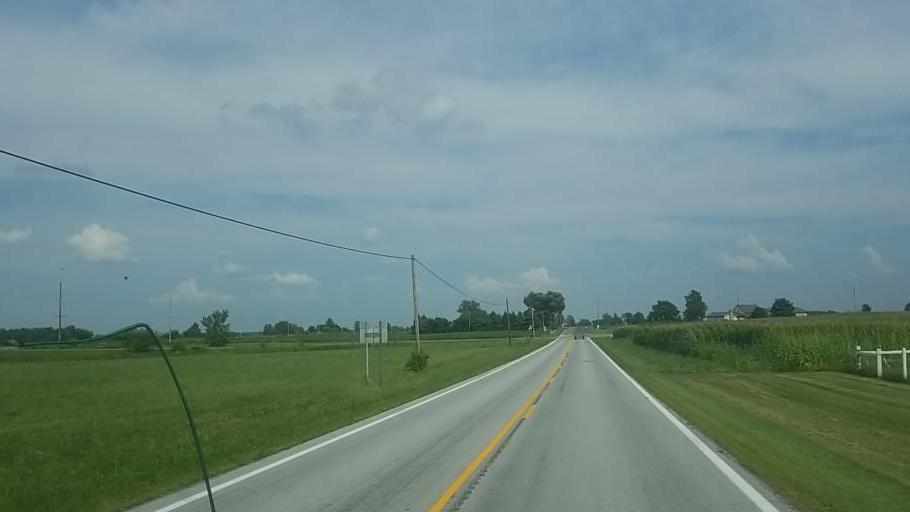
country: US
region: Ohio
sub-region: Hardin County
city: Forest
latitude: 40.8036
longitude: -83.4895
